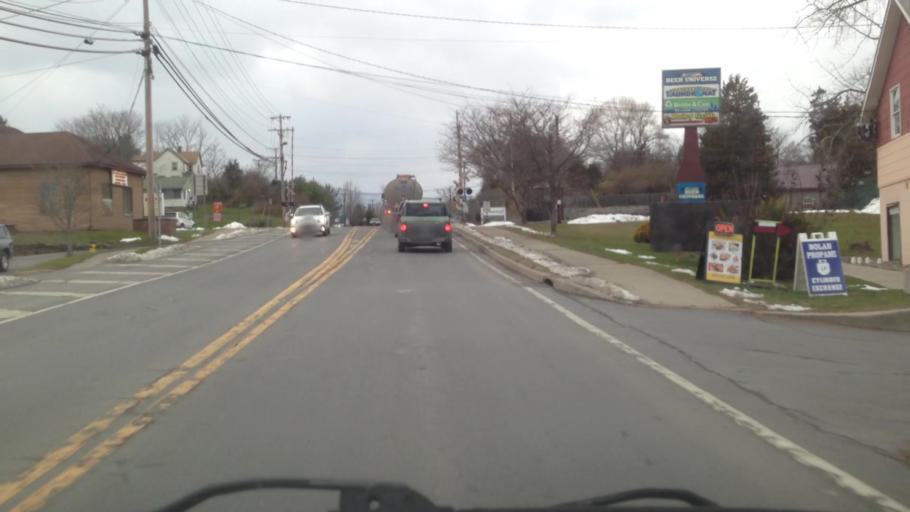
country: US
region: New York
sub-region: Ulster County
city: Saugerties
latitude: 42.0821
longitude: -73.9648
